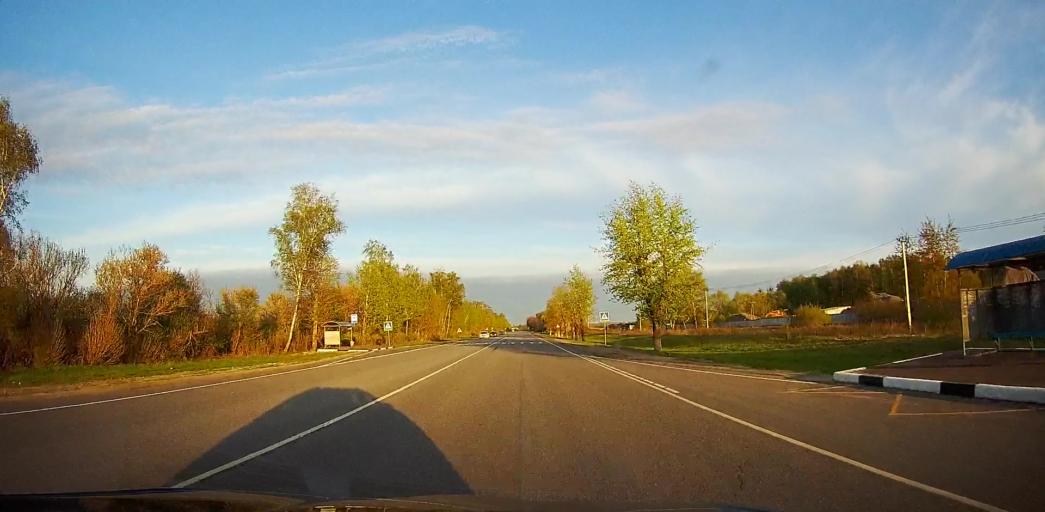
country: RU
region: Moskovskaya
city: Troitskoye
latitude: 55.2159
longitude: 38.5923
